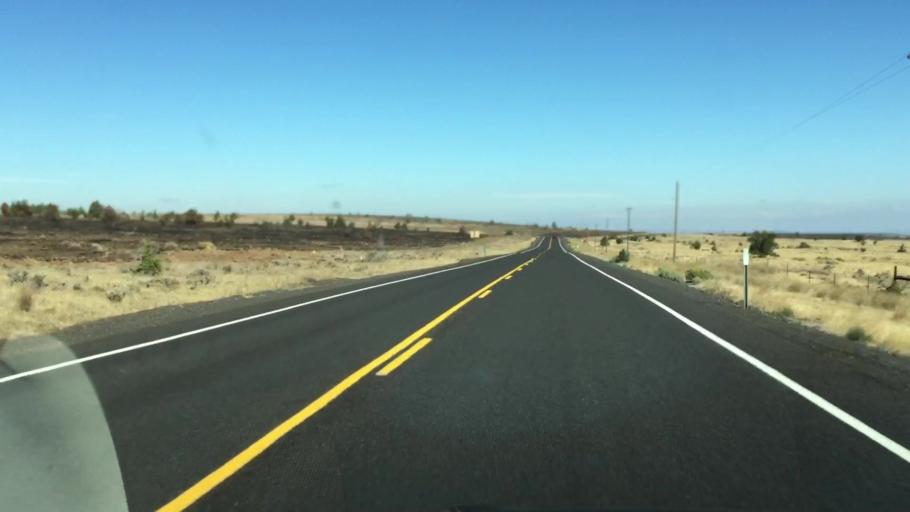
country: US
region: Oregon
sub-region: Jefferson County
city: Warm Springs
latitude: 44.9847
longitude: -120.9927
